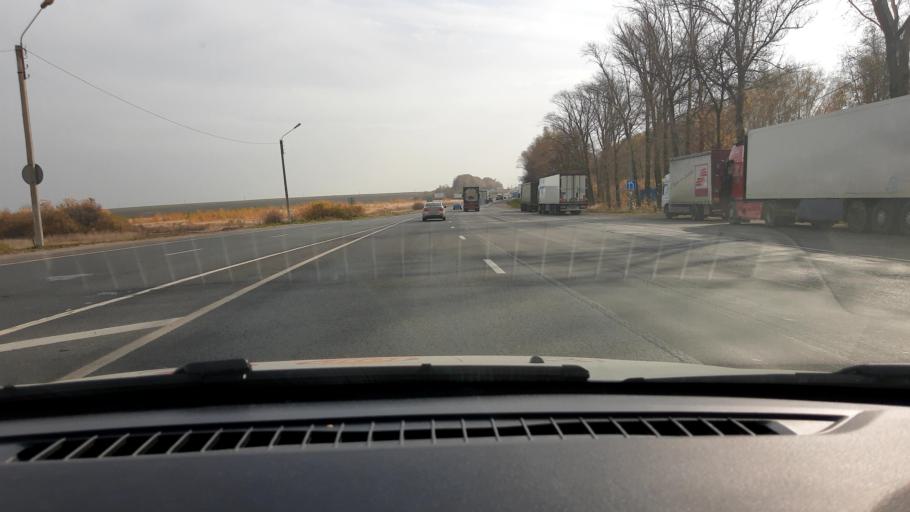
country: RU
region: Nizjnij Novgorod
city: Kstovo
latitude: 56.1234
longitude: 44.2688
